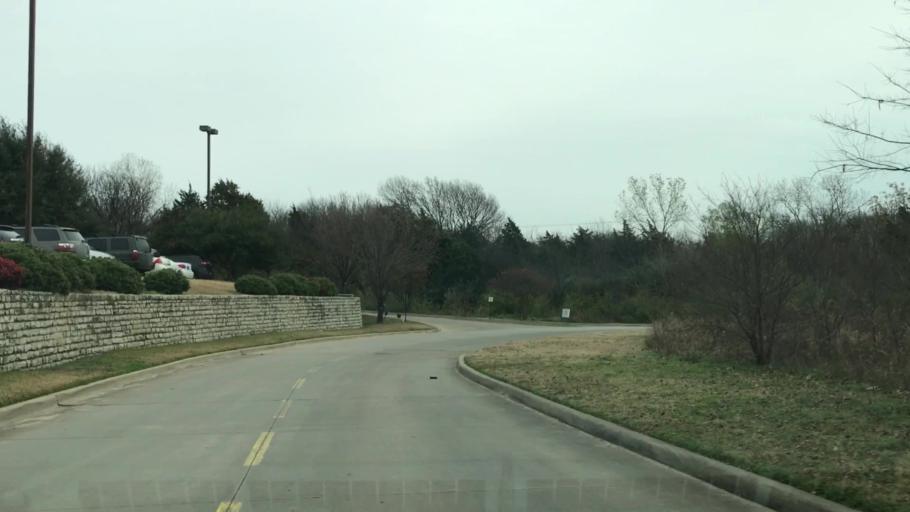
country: US
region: Texas
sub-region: Dallas County
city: Cockrell Hill
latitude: 32.7438
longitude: -96.8954
